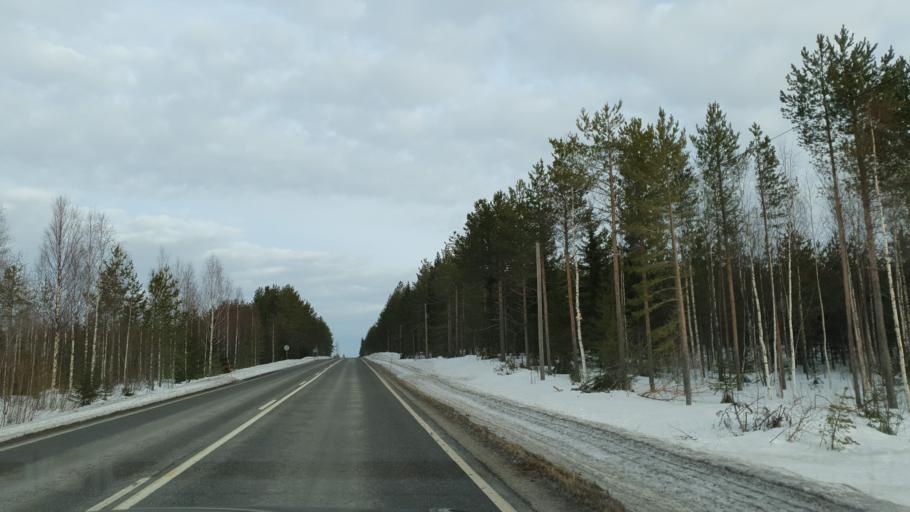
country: FI
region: Kainuu
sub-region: Kajaani
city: Vuokatti
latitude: 64.1833
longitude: 28.1881
